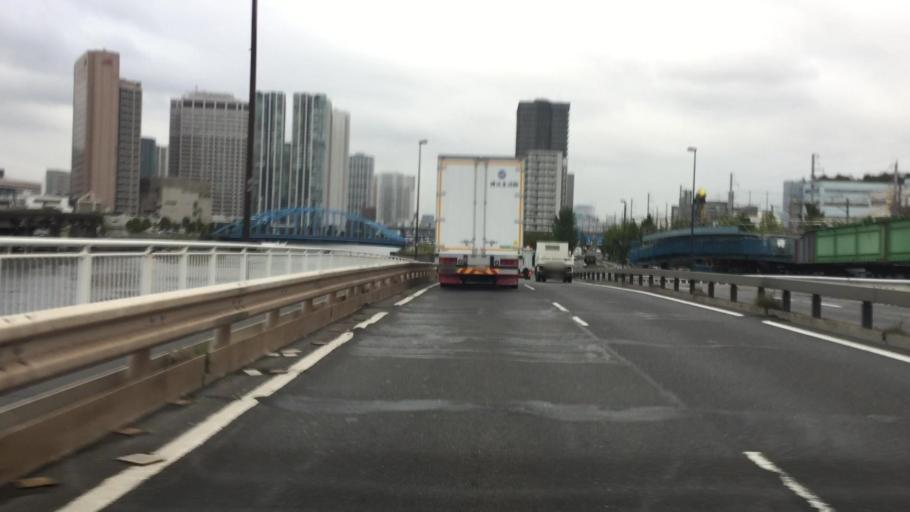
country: JP
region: Tokyo
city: Tokyo
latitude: 35.6184
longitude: 139.7531
